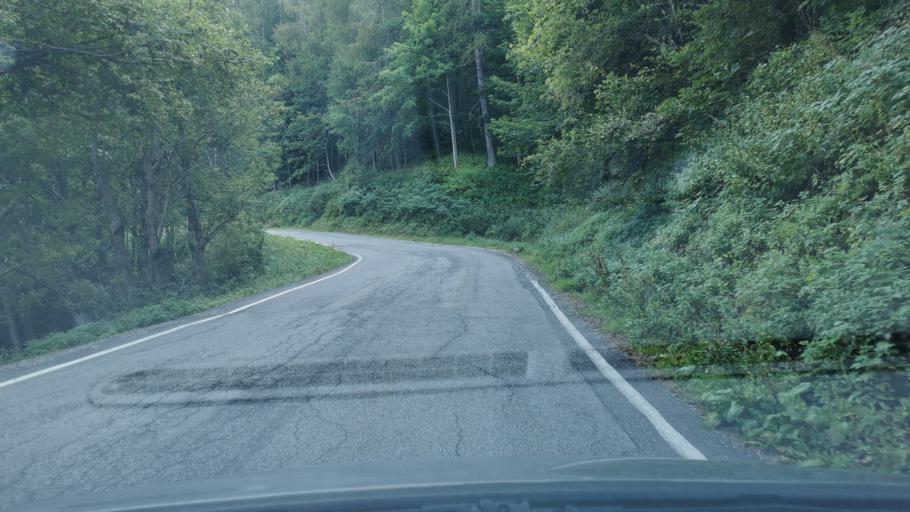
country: IT
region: Piedmont
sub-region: Provincia di Torino
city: Usseglio
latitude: 45.2235
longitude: 7.2215
